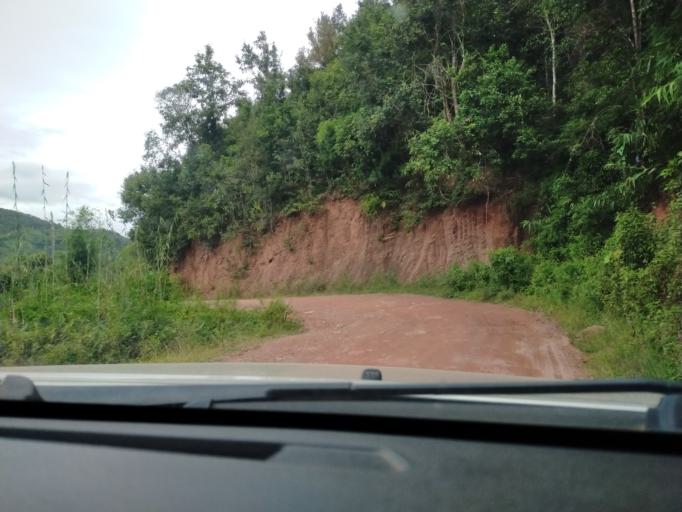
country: TH
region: Nan
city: Chaloem Phra Kiat
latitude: 19.7670
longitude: 101.3486
